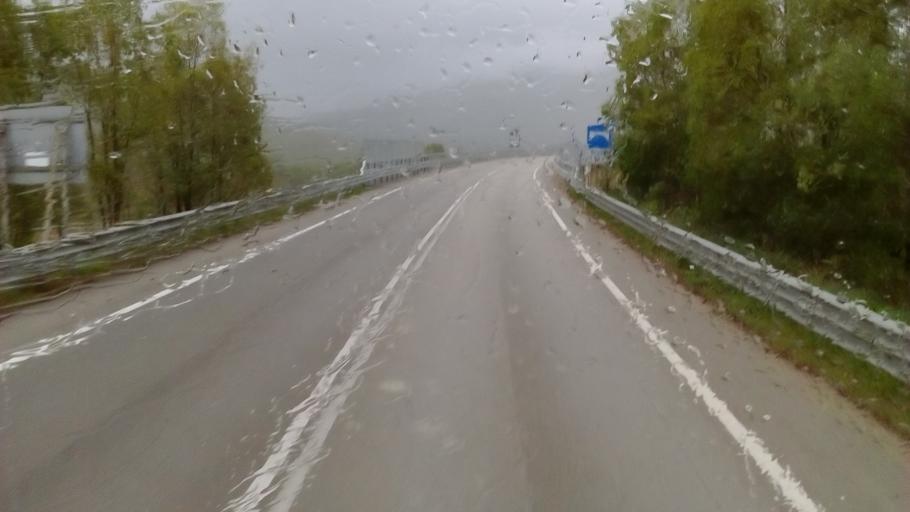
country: IT
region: Sicily
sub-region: Enna
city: Villarosa
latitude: 37.5333
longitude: 14.1298
